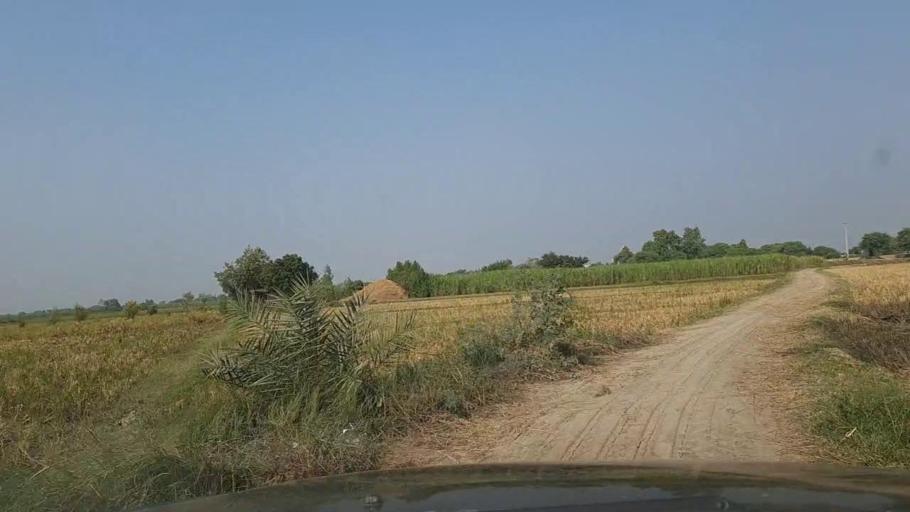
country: PK
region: Sindh
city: Mirpur Batoro
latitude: 24.6970
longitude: 68.2555
